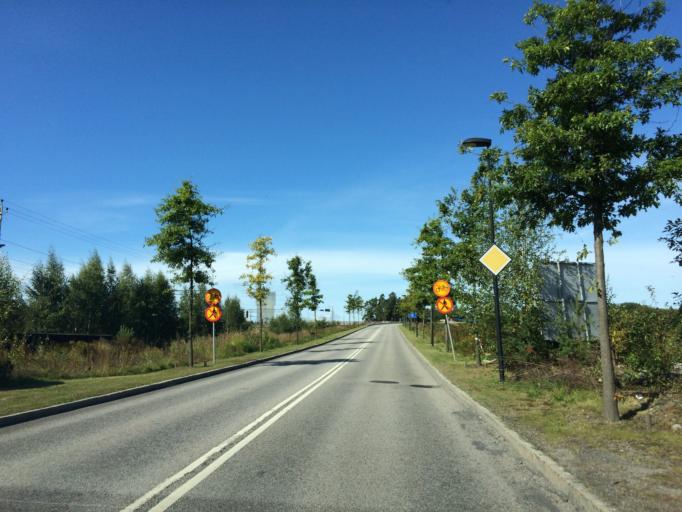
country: SE
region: Stockholm
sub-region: Stockholms Kommun
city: Kista
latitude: 59.4013
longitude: 17.9781
